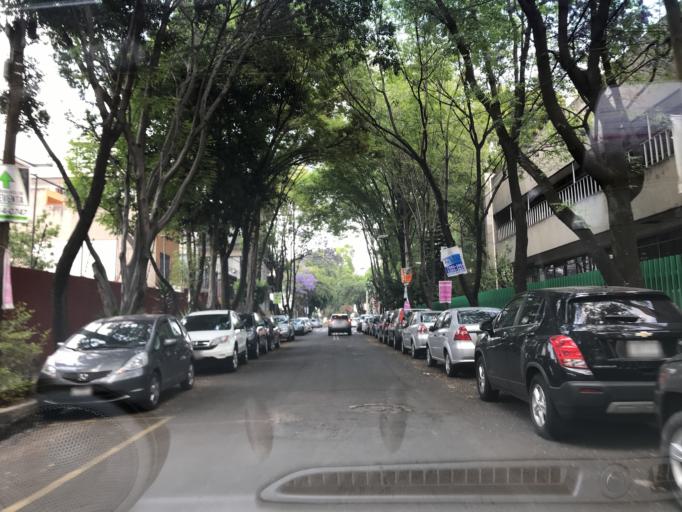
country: MX
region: Mexico City
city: Colonia del Valle
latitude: 19.3837
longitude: -99.1656
